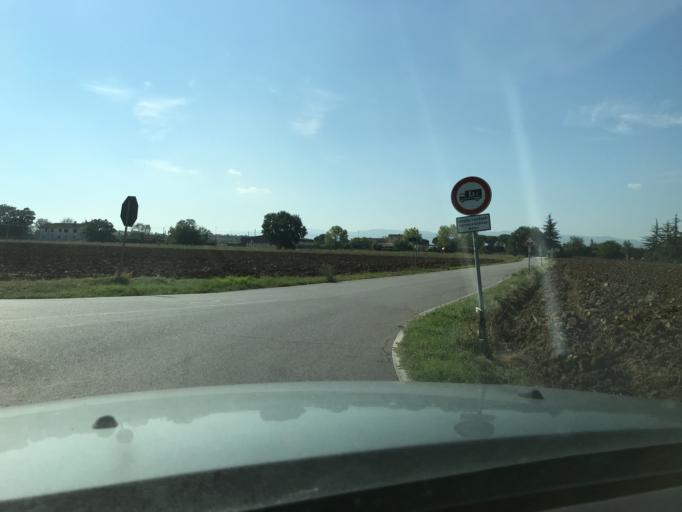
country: IT
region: Umbria
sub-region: Provincia di Perugia
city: Ospedalicchio
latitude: 43.0866
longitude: 12.5081
